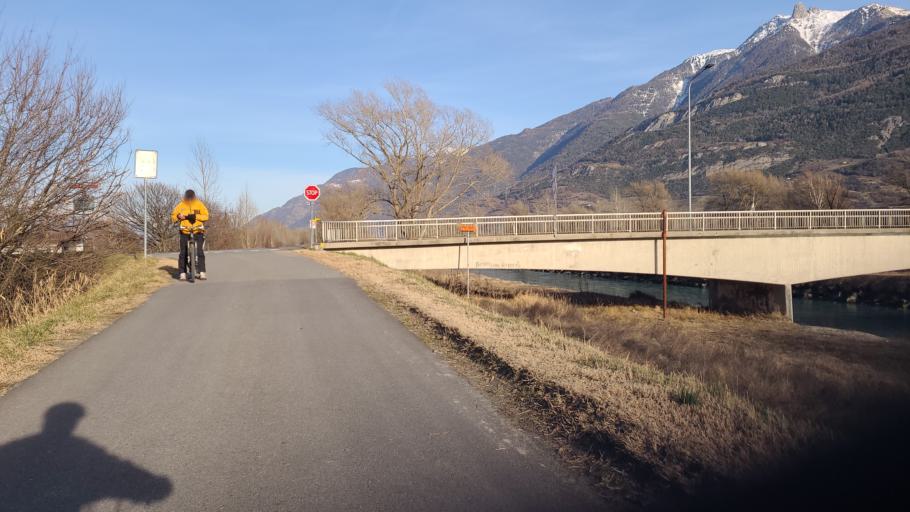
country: CH
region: Valais
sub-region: Martigny District
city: Fully
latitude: 46.1354
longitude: 7.1214
